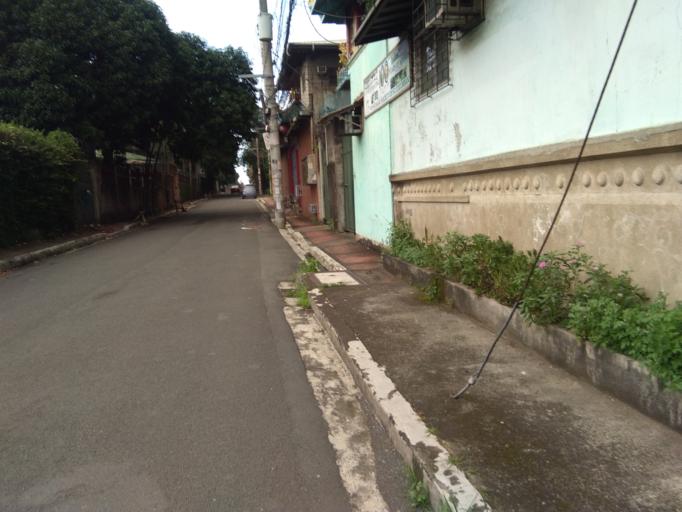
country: PH
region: Metro Manila
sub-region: San Juan
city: San Juan
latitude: 14.6197
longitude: 121.0422
